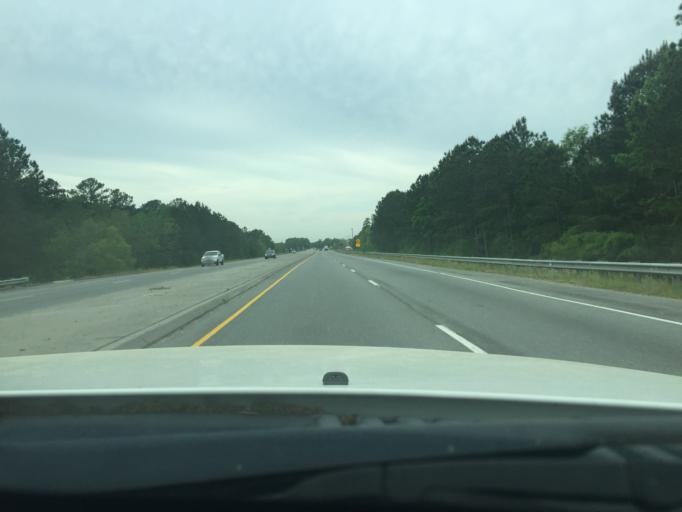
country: US
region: Georgia
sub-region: Bryan County
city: Richmond Hill
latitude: 31.9838
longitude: -81.2838
